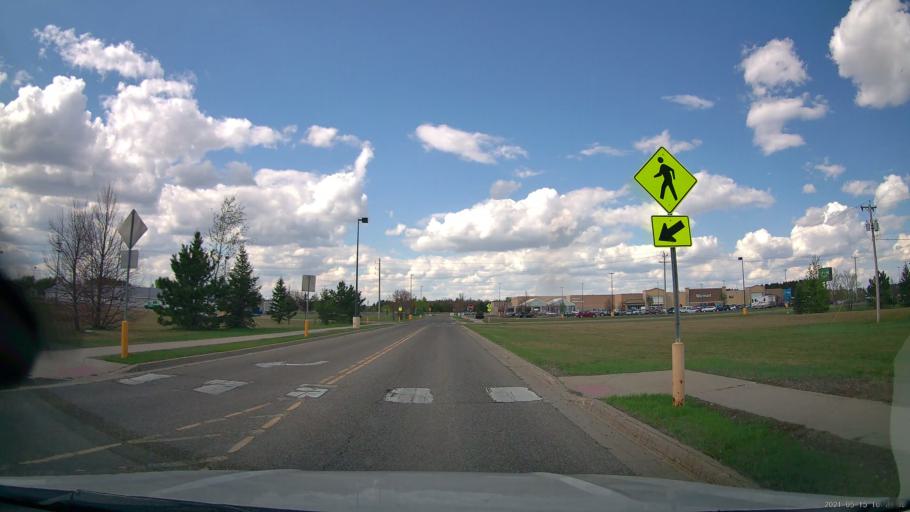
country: US
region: Minnesota
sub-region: Hubbard County
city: Park Rapids
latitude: 46.9230
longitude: -95.0353
